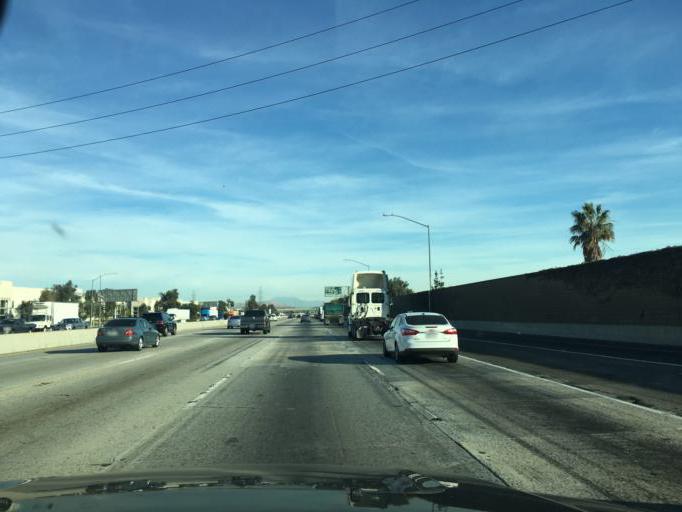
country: US
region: California
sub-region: Riverside County
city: Mira Loma
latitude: 34.0280
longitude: -117.5729
